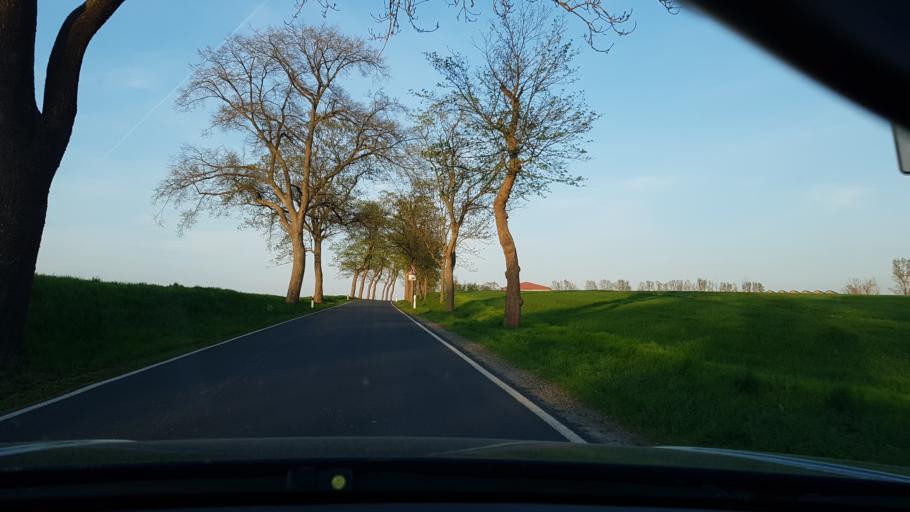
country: DE
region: Mecklenburg-Vorpommern
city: Alt-Sanitz
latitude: 53.8960
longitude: 13.5742
